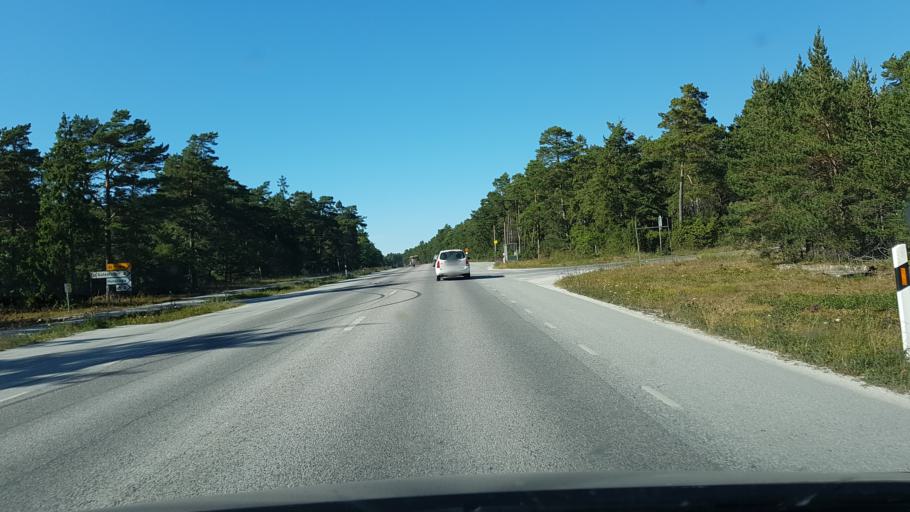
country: SE
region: Gotland
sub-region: Gotland
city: Vibble
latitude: 57.5524
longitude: 18.2029
